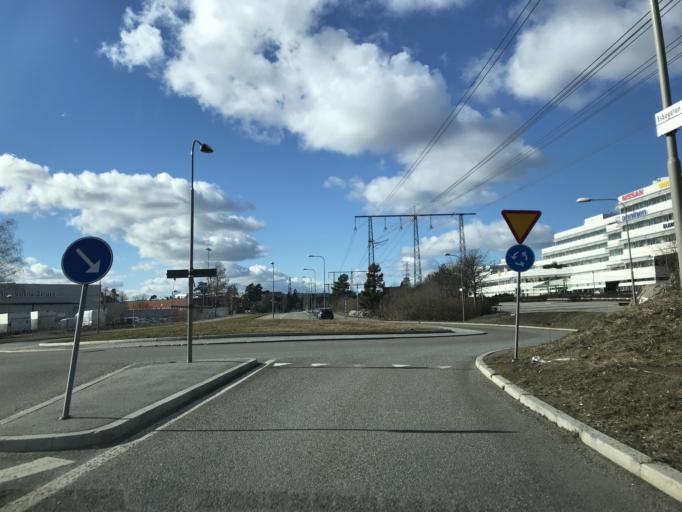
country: SE
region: Stockholm
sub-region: Stockholms Kommun
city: Kista
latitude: 59.4179
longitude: 17.9289
